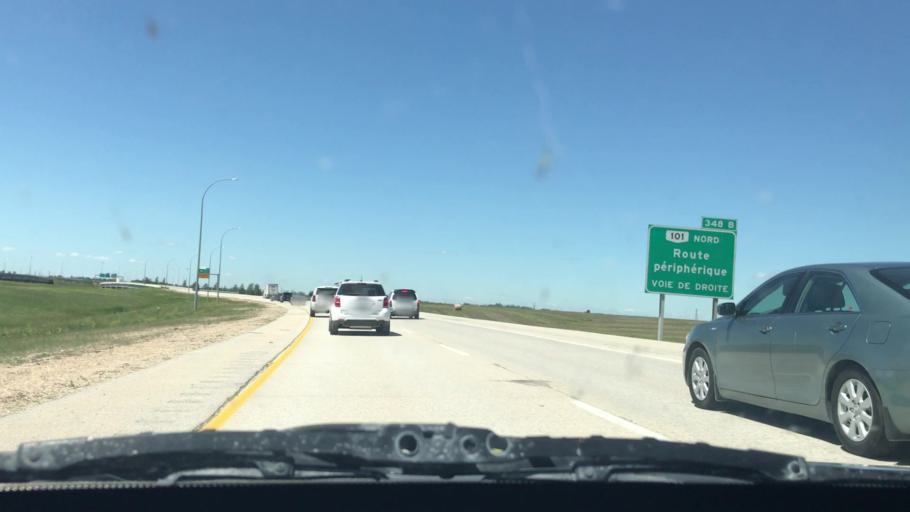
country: CA
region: Manitoba
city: Winnipeg
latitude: 49.8287
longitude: -96.9479
